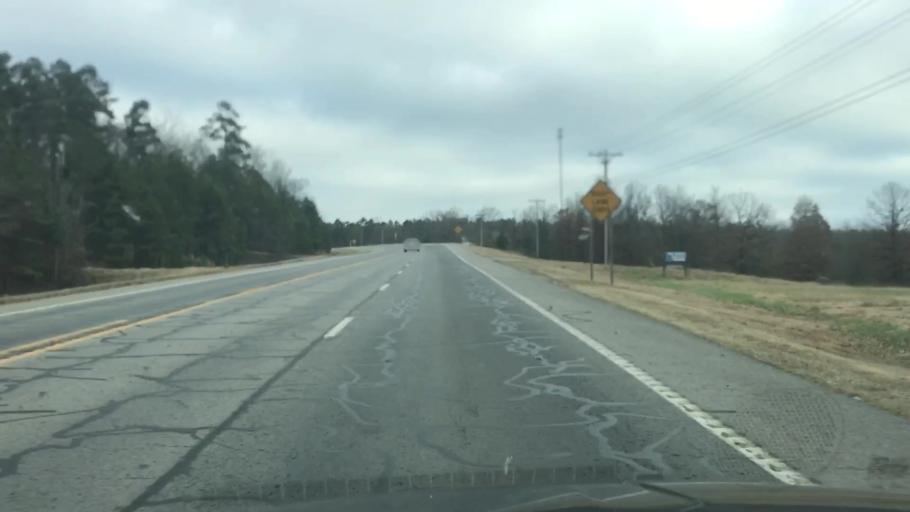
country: US
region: Arkansas
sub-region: Scott County
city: Waldron
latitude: 34.8163
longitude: -94.0384
